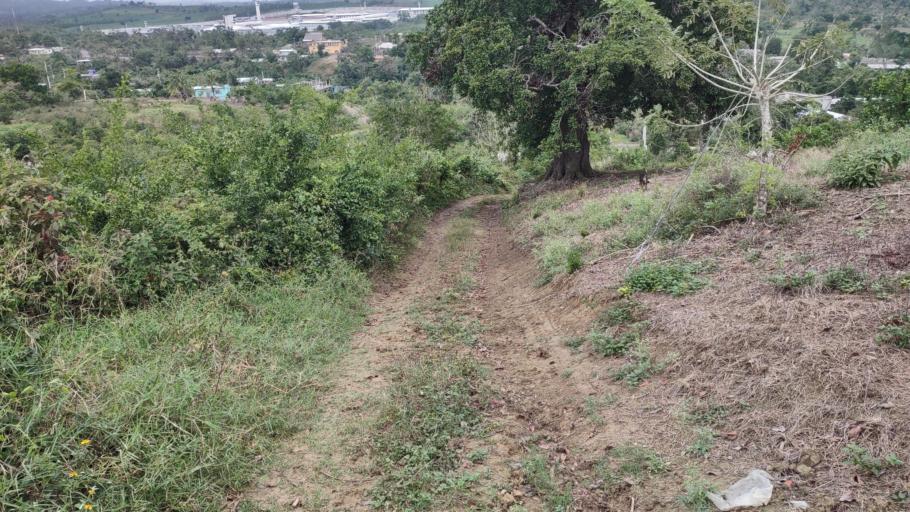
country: MX
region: Veracruz
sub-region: Papantla
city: El Chote
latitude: 20.3930
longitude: -97.3939
